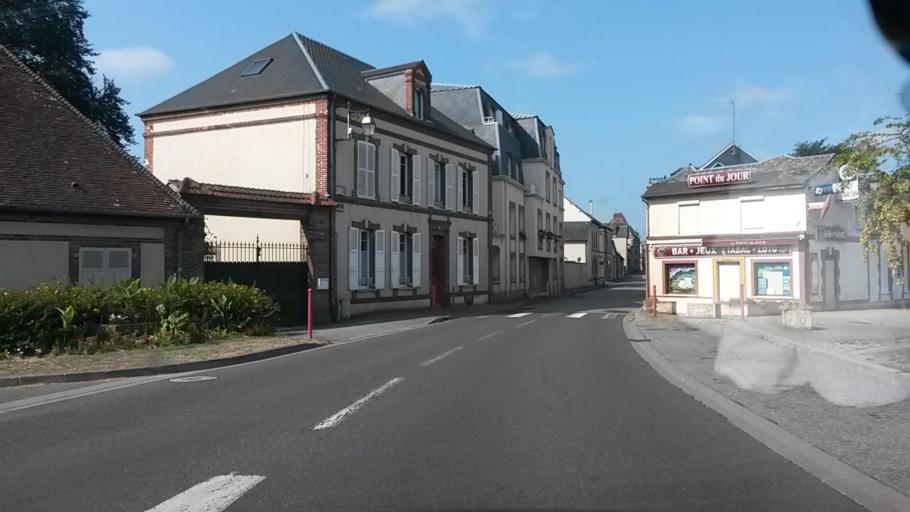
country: FR
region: Haute-Normandie
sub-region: Departement de l'Eure
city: Damville
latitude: 48.8712
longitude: 1.0789
